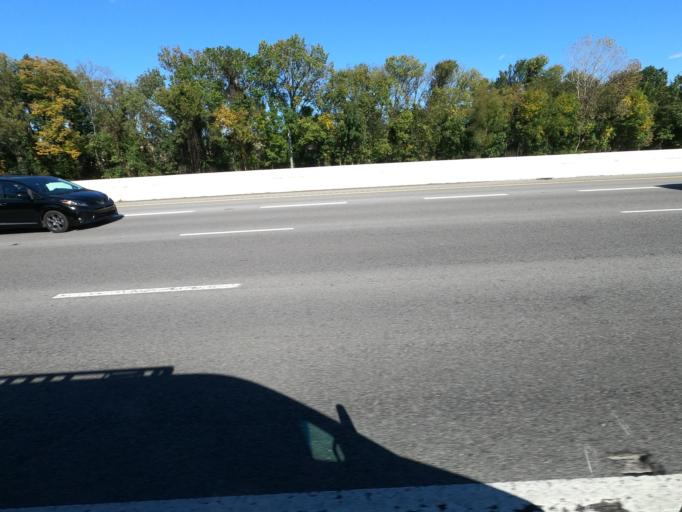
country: US
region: Tennessee
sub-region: Rutherford County
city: Murfreesboro
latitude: 35.8524
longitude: -86.4415
